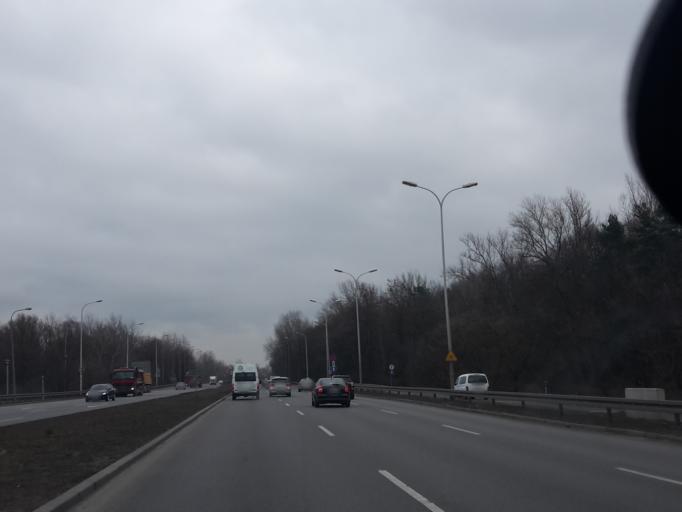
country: PL
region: Masovian Voivodeship
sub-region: Warszawa
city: Bielany
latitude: 52.3013
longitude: 20.9501
